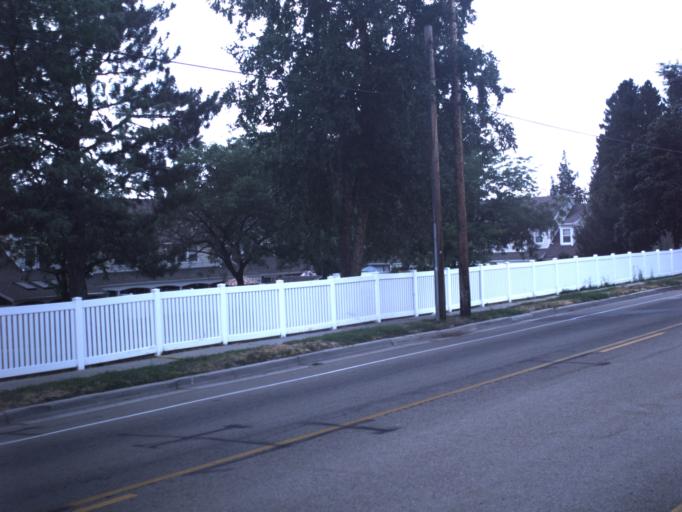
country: US
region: Utah
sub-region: Davis County
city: Centerville
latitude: 40.9267
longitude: -111.8789
